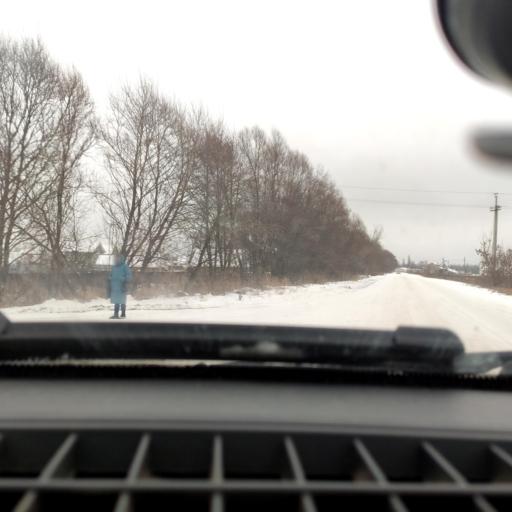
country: RU
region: Bashkortostan
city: Mikhaylovka
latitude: 54.7741
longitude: 55.8219
